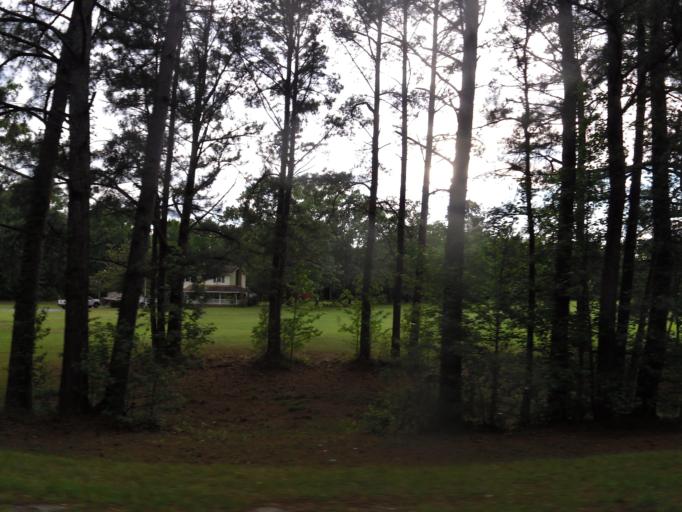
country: US
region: South Carolina
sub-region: Jasper County
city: Hardeeville
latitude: 32.3262
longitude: -81.0899
